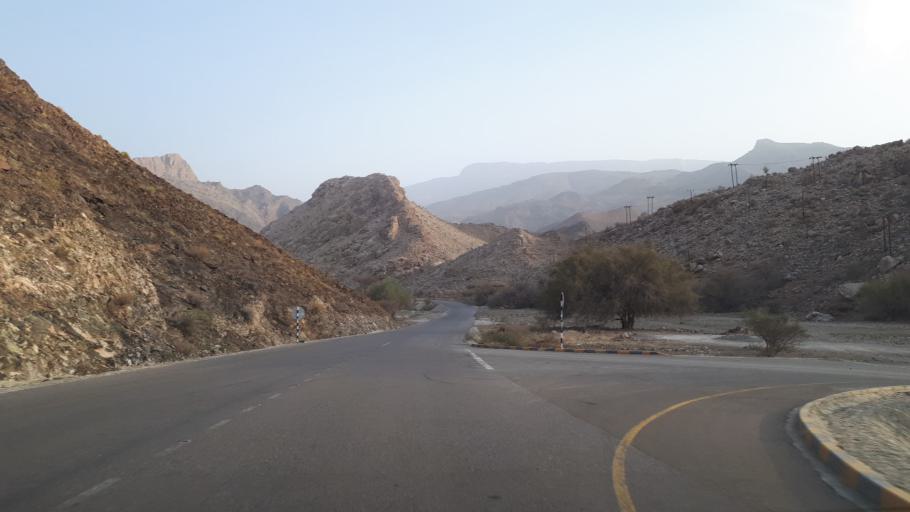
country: OM
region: Al Batinah
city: Rustaq
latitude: 23.4174
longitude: 57.1687
